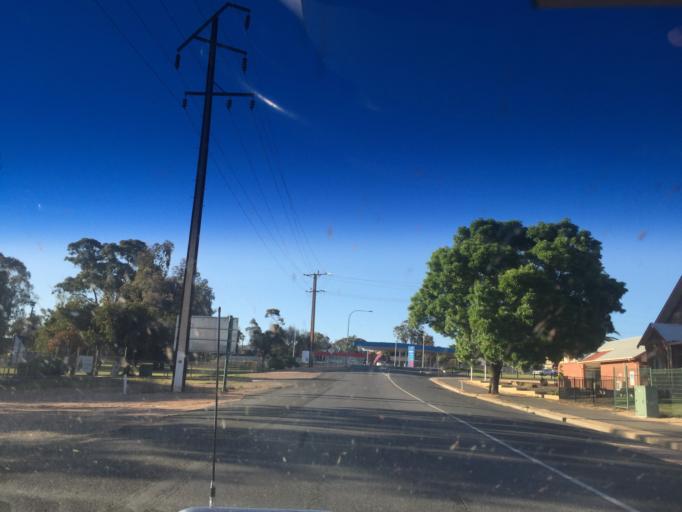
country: AU
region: South Australia
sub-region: Berri and Barmera
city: Berri
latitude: -34.2847
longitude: 140.5969
